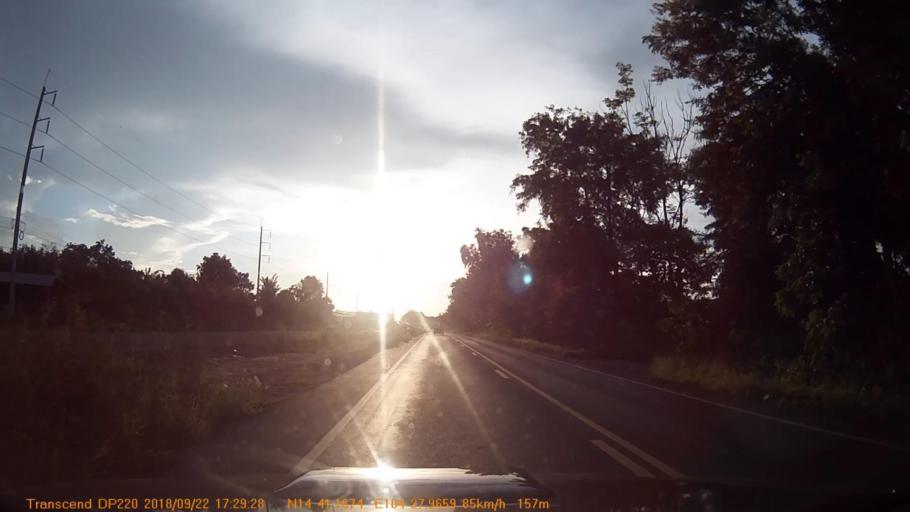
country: TH
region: Sisaket
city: Khun Han
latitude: 14.6861
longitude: 104.4658
